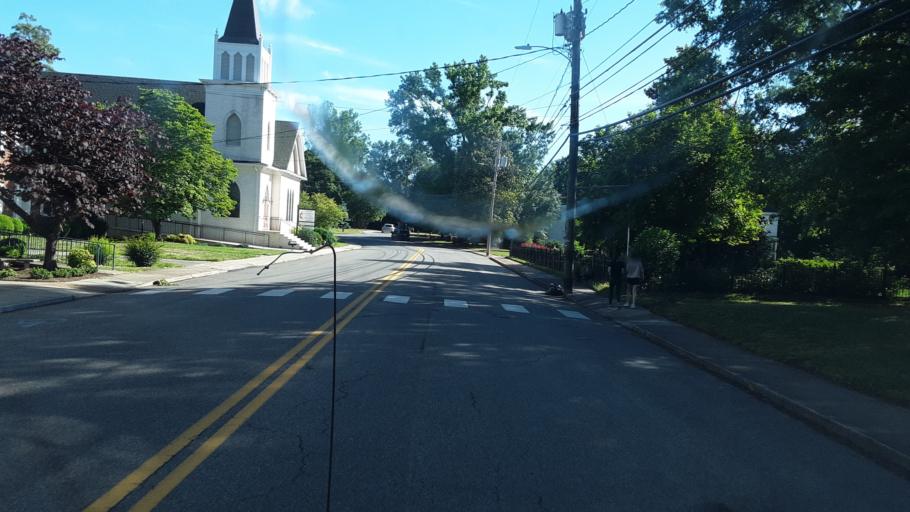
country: US
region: Virginia
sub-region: Pittsylvania County
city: Chatham
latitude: 36.8291
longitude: -79.3971
